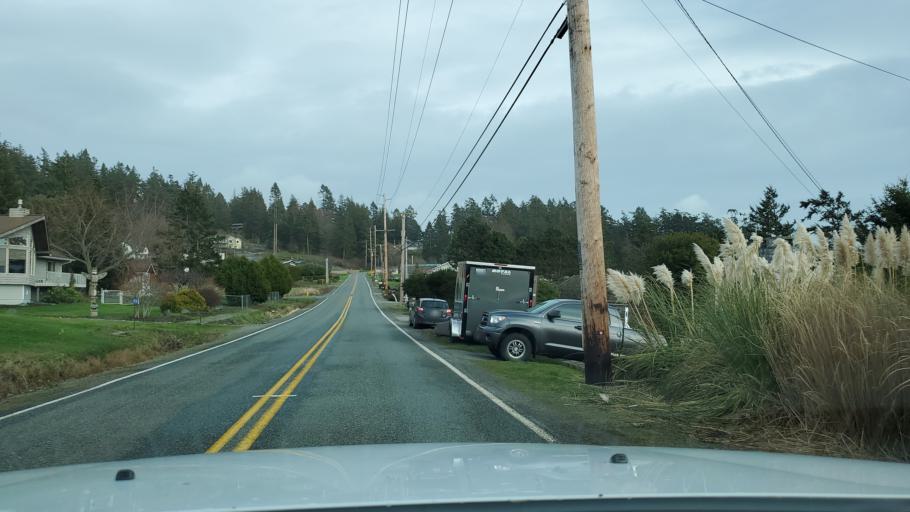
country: US
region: Washington
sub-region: Skagit County
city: Anacortes
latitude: 48.4250
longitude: -122.6051
